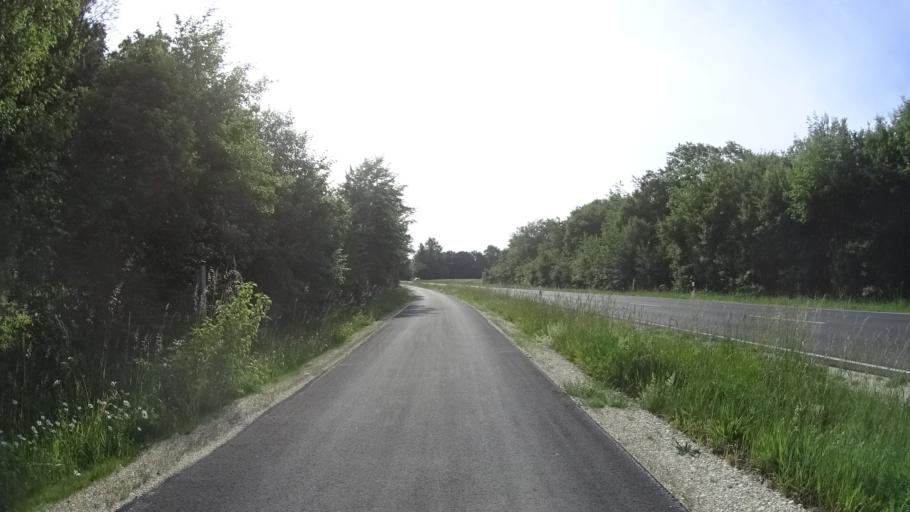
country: DE
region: Bavaria
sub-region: Lower Bavaria
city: Essing
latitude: 48.9269
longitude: 11.8226
